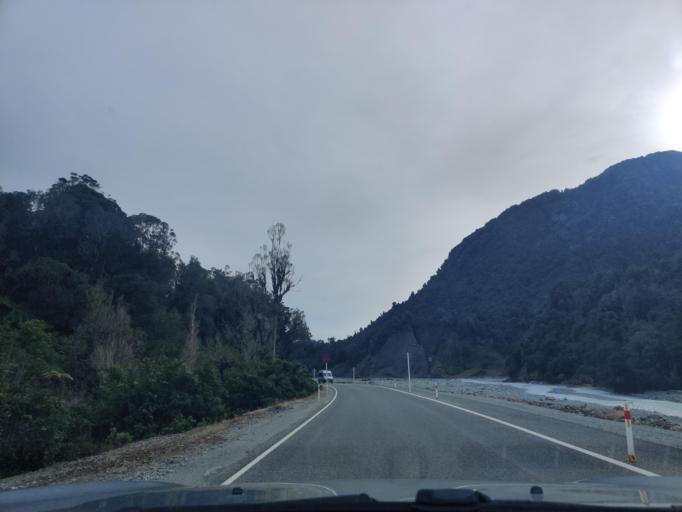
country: NZ
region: West Coast
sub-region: Westland District
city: Hokitika
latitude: -43.4028
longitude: 170.1789
